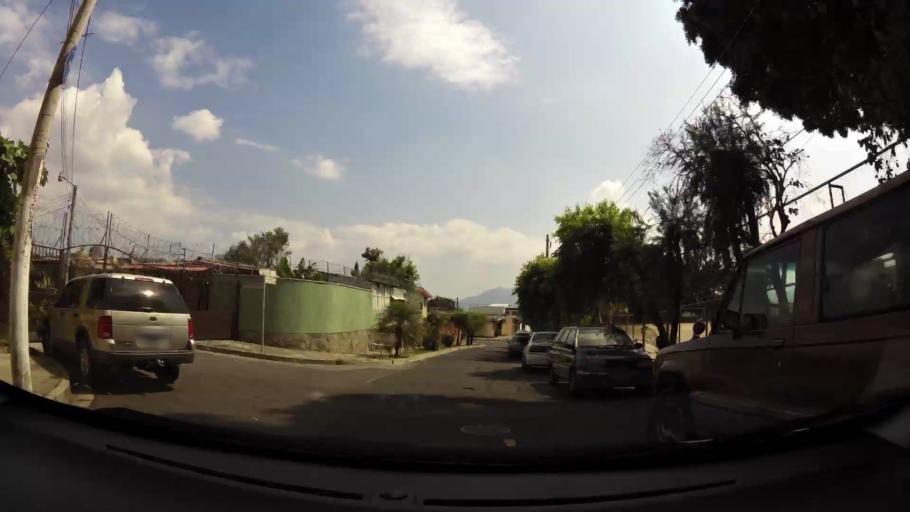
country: SV
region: San Salvador
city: Mejicanos
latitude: 13.7117
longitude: -89.2200
